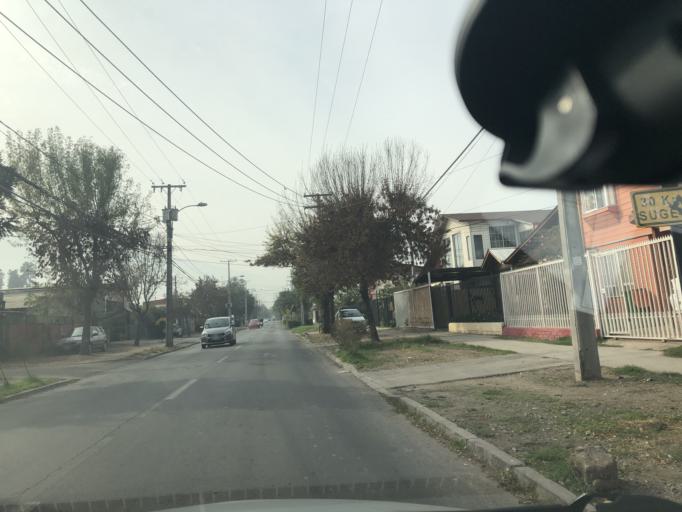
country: CL
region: Santiago Metropolitan
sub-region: Provincia de Cordillera
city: Puente Alto
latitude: -33.5805
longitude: -70.5793
